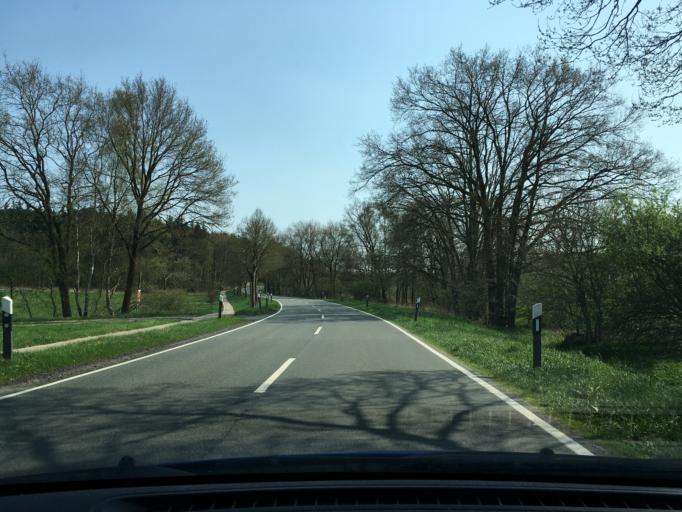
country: DE
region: Lower Saxony
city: Sudergellersen
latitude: 53.1984
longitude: 10.3047
